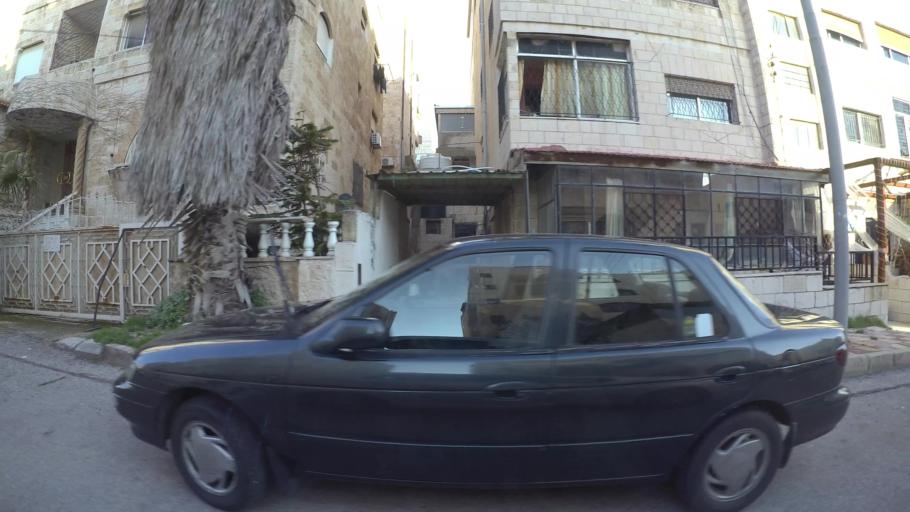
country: JO
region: Amman
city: Al Jubayhah
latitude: 31.9956
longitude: 35.8670
